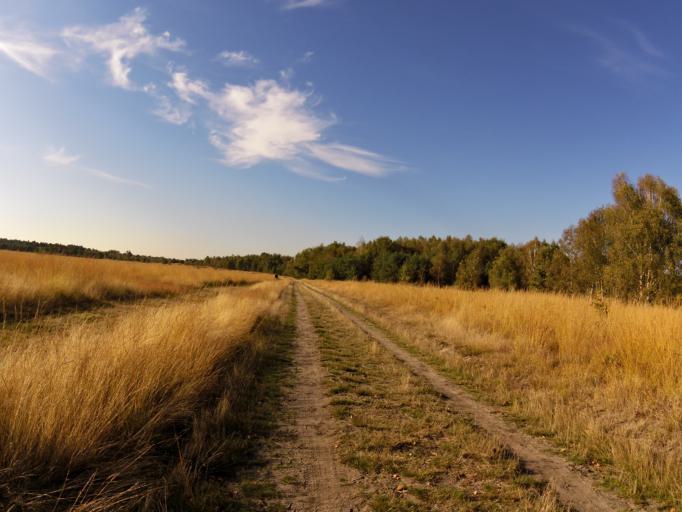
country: NL
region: Limburg
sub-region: Gemeente Bergen
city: Wellerlooi
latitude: 51.5260
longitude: 6.1757
